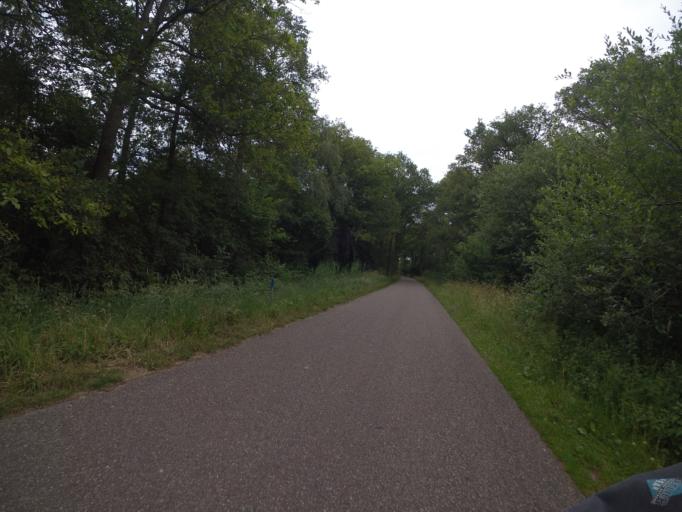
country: NL
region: North Brabant
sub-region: Gemeente Oirschot
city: Oirschot
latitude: 51.5311
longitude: 5.3509
